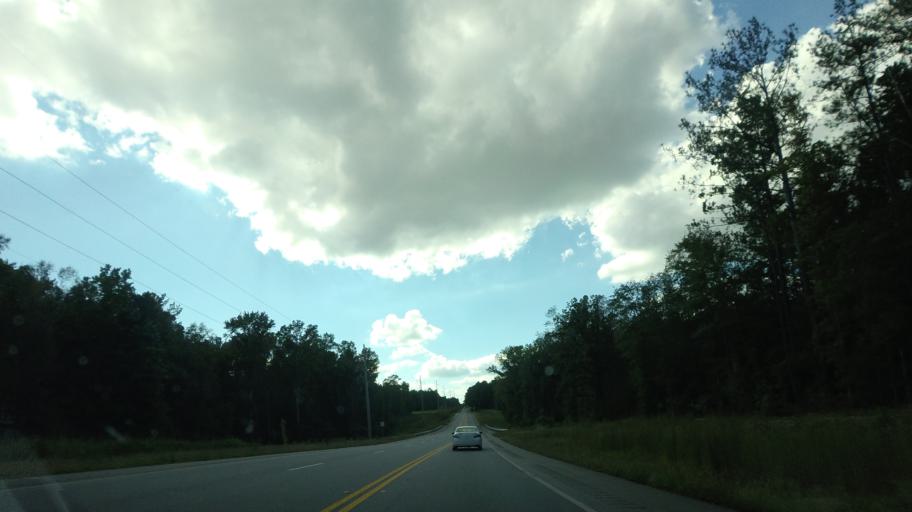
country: US
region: Georgia
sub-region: Lamar County
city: Barnesville
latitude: 33.0541
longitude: -84.0692
